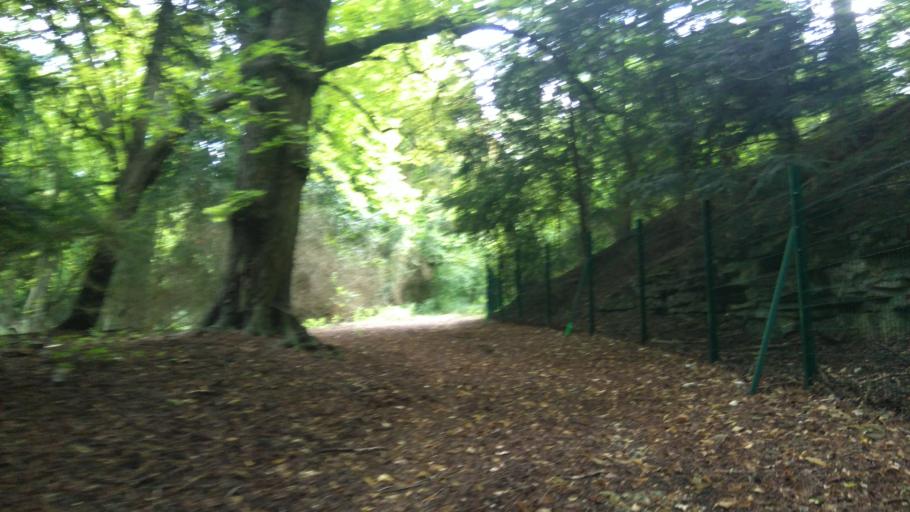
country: FR
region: Picardie
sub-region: Departement de l'Oise
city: Saint-Maximin
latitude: 49.2350
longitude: 2.4496
